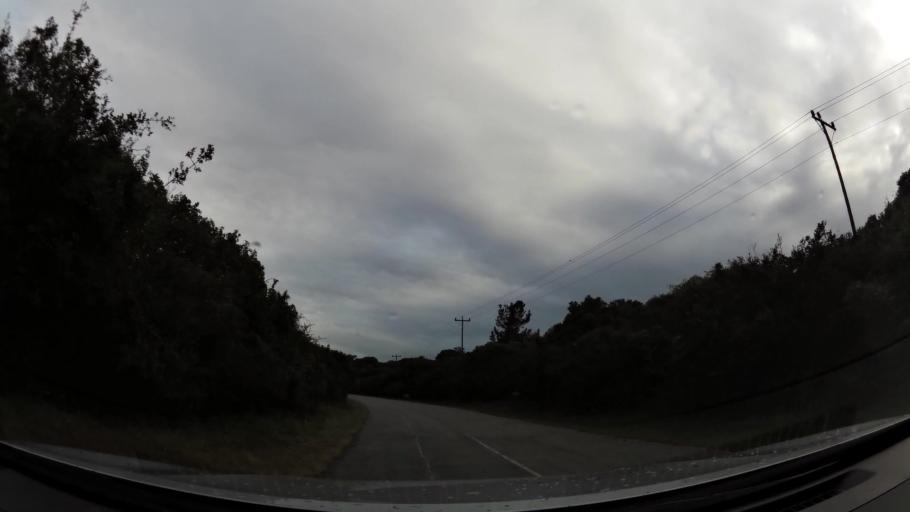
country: ZA
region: Eastern Cape
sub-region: Nelson Mandela Bay Metropolitan Municipality
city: Port Elizabeth
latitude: -34.0106
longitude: 25.4956
